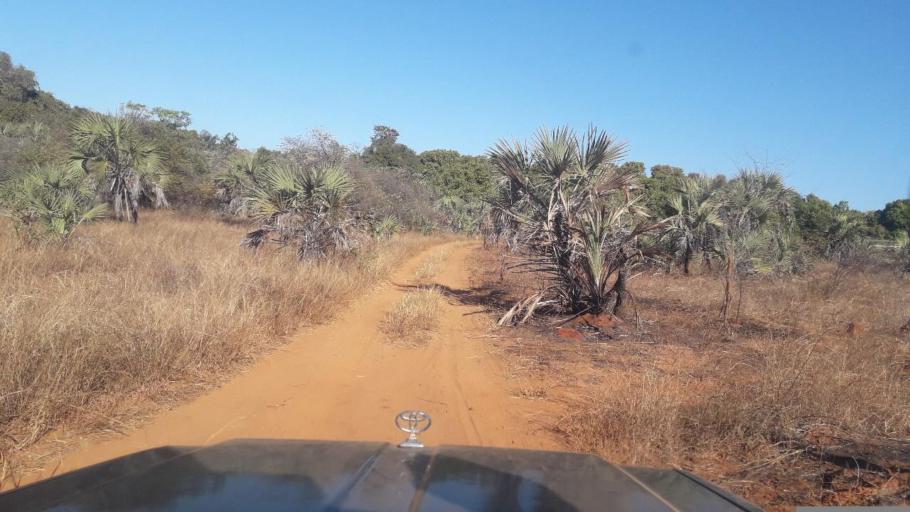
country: MG
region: Boeny
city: Sitampiky
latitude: -16.4048
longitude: 45.5985
